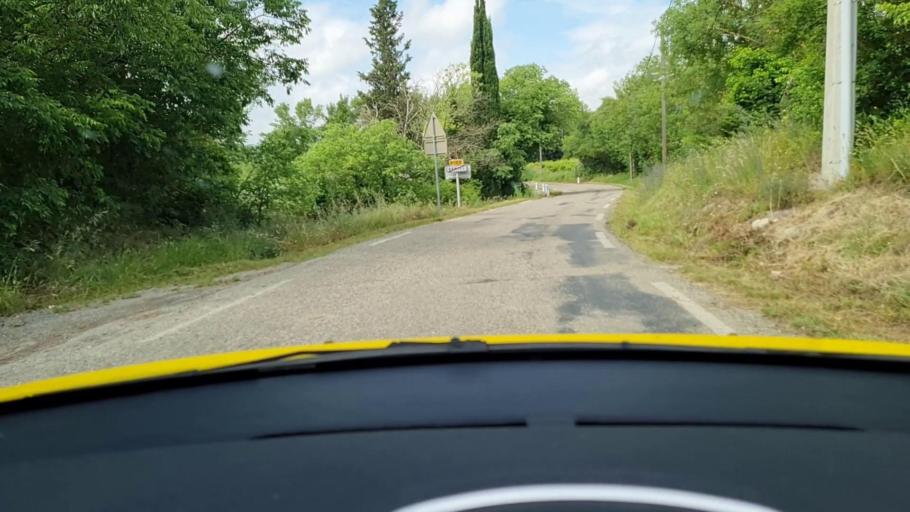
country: FR
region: Languedoc-Roussillon
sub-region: Departement du Gard
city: Quissac
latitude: 43.8457
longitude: 4.0046
